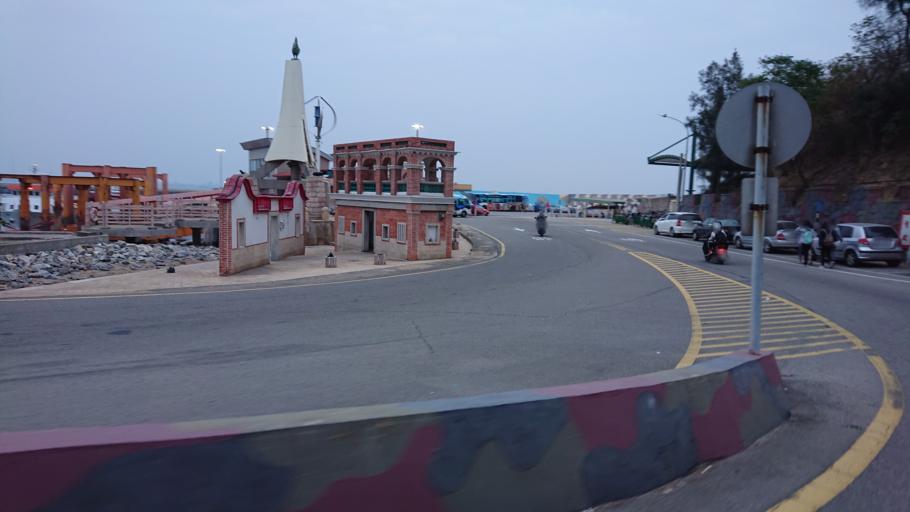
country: TW
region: Fukien
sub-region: Kinmen
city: Jincheng
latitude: 24.4254
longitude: 118.2623
